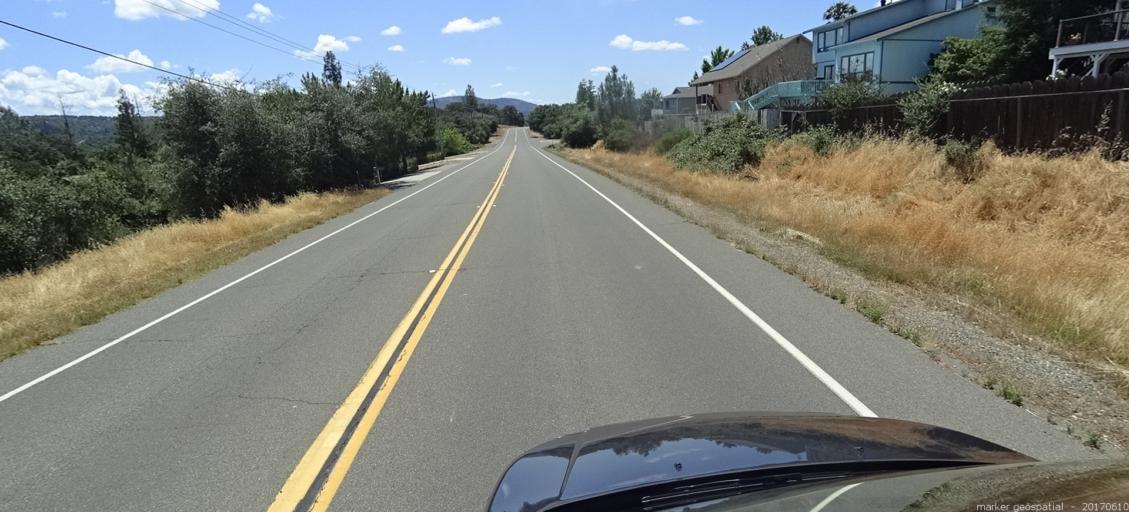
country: US
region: California
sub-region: Butte County
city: Oroville East
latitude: 39.5197
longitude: -121.4668
